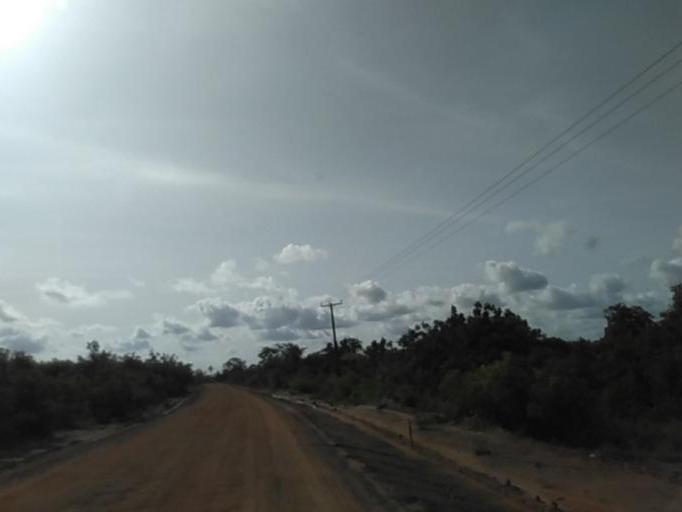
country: GH
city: Akropong
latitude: 6.0830
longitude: 0.2763
